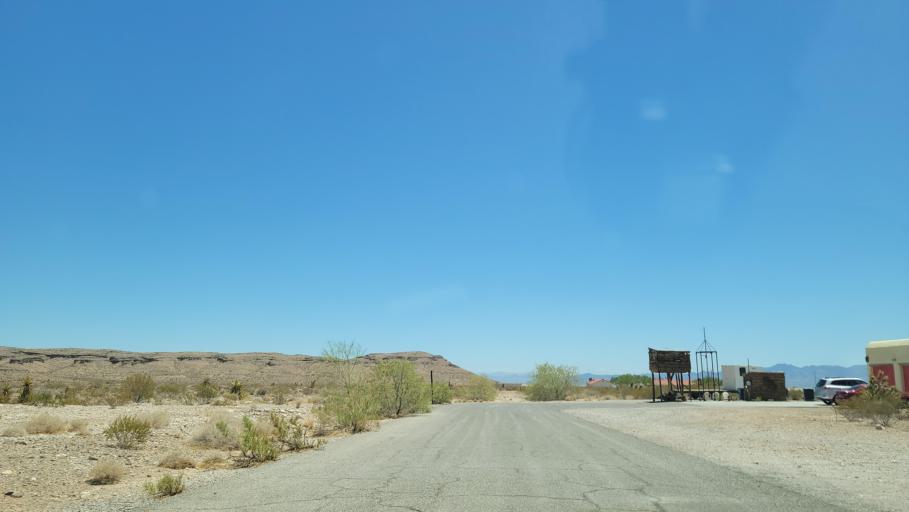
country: US
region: Nevada
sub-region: Clark County
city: Summerlin South
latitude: 36.0335
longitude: -115.3399
